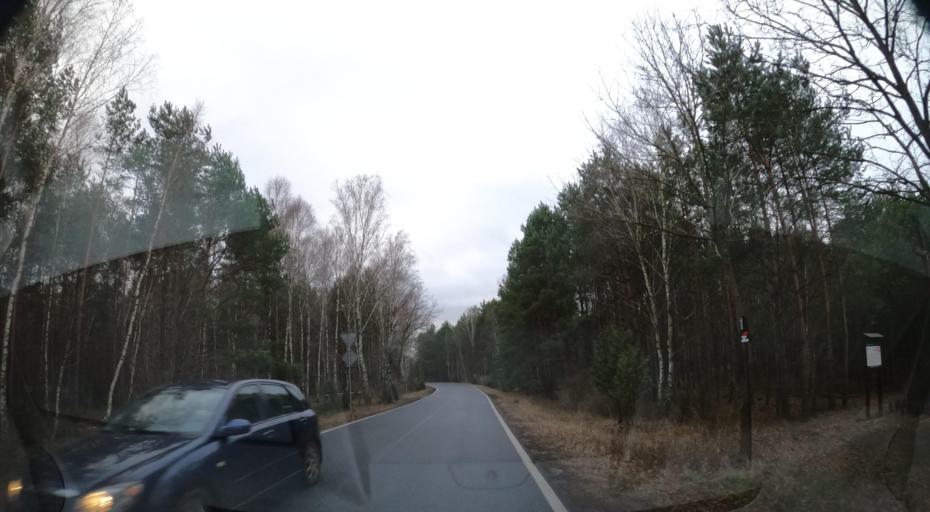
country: PL
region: Kujawsko-Pomorskie
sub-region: Powiat bydgoski
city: Solec Kujawski
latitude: 53.0578
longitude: 18.2282
